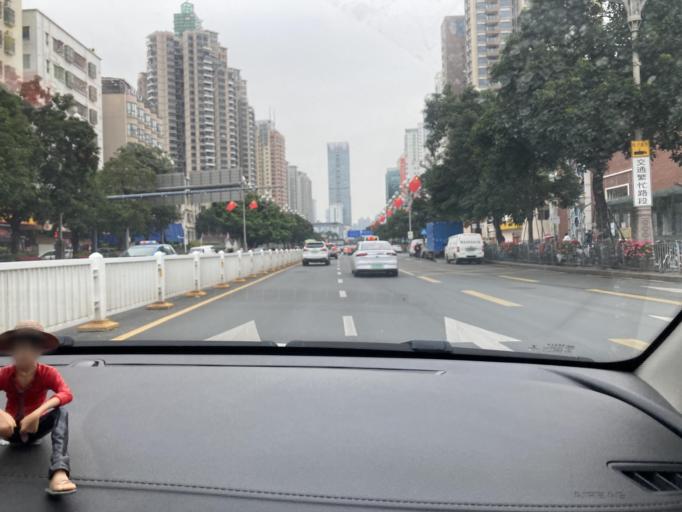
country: CN
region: Guangdong
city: Nantou
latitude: 22.5353
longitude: 113.9106
